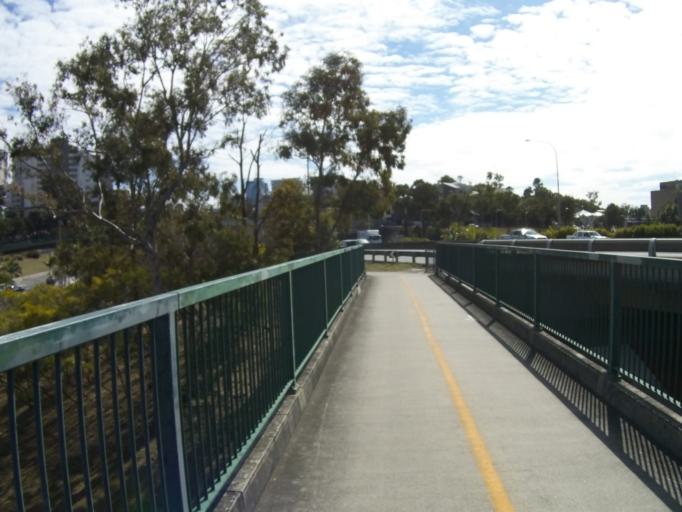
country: AU
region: Queensland
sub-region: Brisbane
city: Woolloongabba
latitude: -27.4858
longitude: 153.0316
